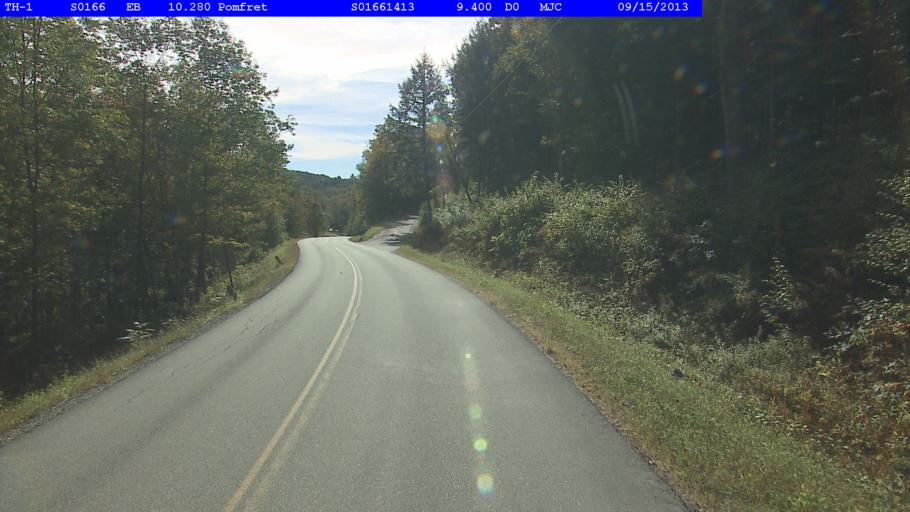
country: US
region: Vermont
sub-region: Windsor County
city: Woodstock
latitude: 43.7205
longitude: -72.4392
